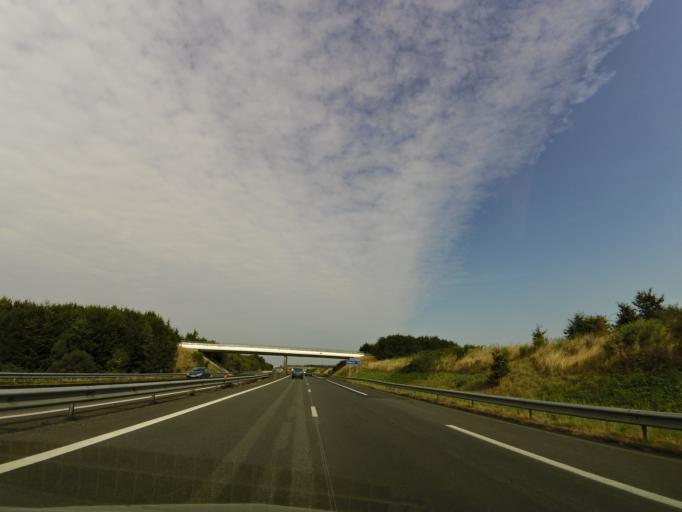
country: FR
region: Pays de la Loire
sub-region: Departement de la Loire-Atlantique
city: Aigrefeuille-sur-Maine
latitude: 47.0783
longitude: -1.4431
